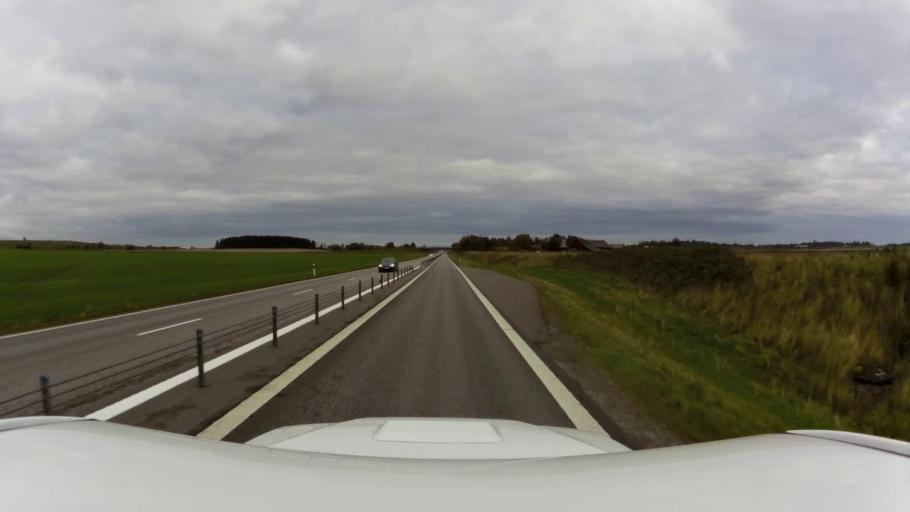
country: SE
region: OEstergoetland
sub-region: Linkopings Kommun
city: Berg
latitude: 58.4642
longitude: 15.4957
